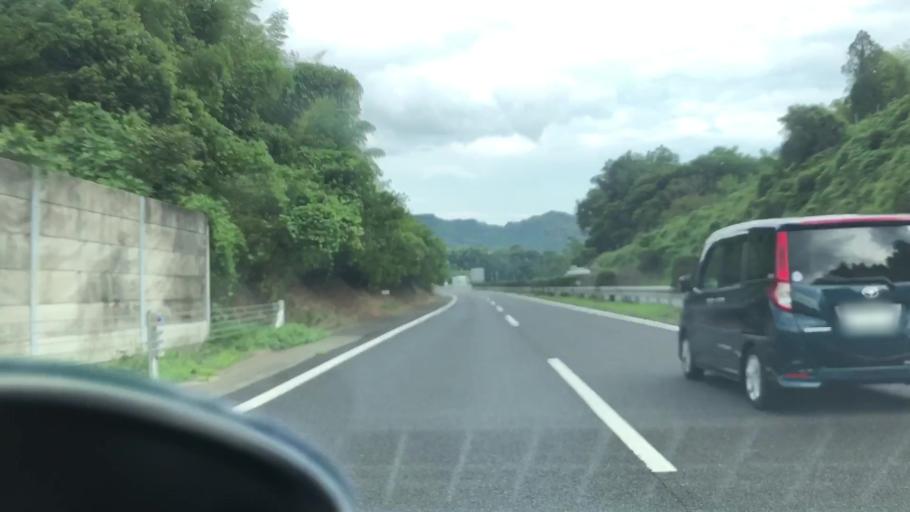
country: JP
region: Hyogo
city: Yamazakicho-nakabirose
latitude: 34.9659
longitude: 134.6776
